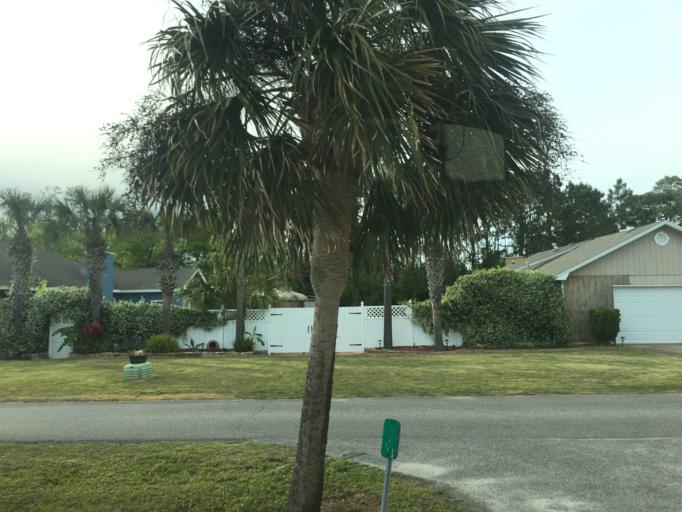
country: US
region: Florida
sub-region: Bay County
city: Panama City Beach
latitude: 30.1763
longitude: -85.7727
